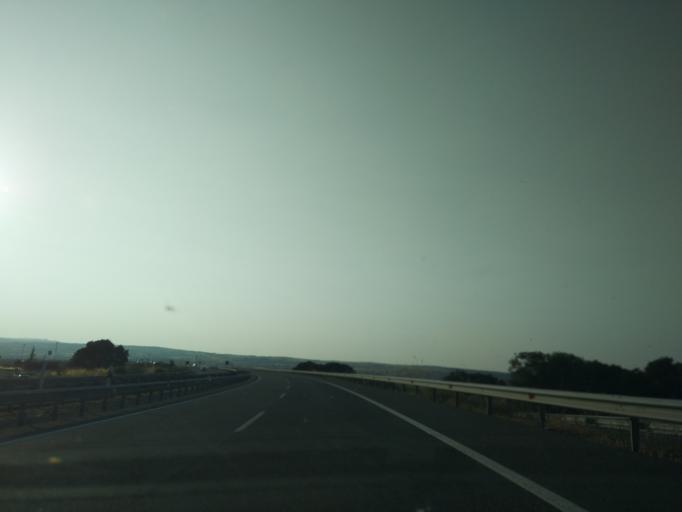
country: ES
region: Castille and Leon
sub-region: Provincia de Avila
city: Avila
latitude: 40.6760
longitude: -4.6826
